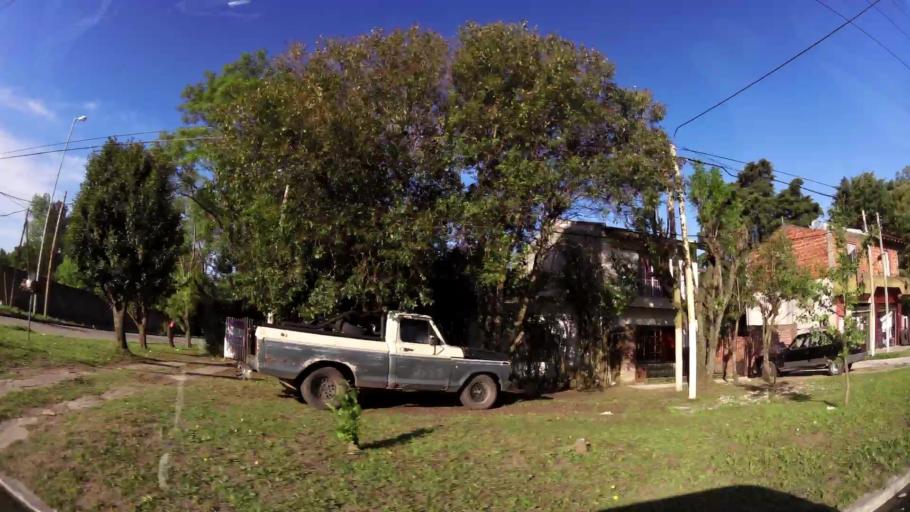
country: AR
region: Buenos Aires
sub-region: Partido de Quilmes
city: Quilmes
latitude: -34.8086
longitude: -58.2044
